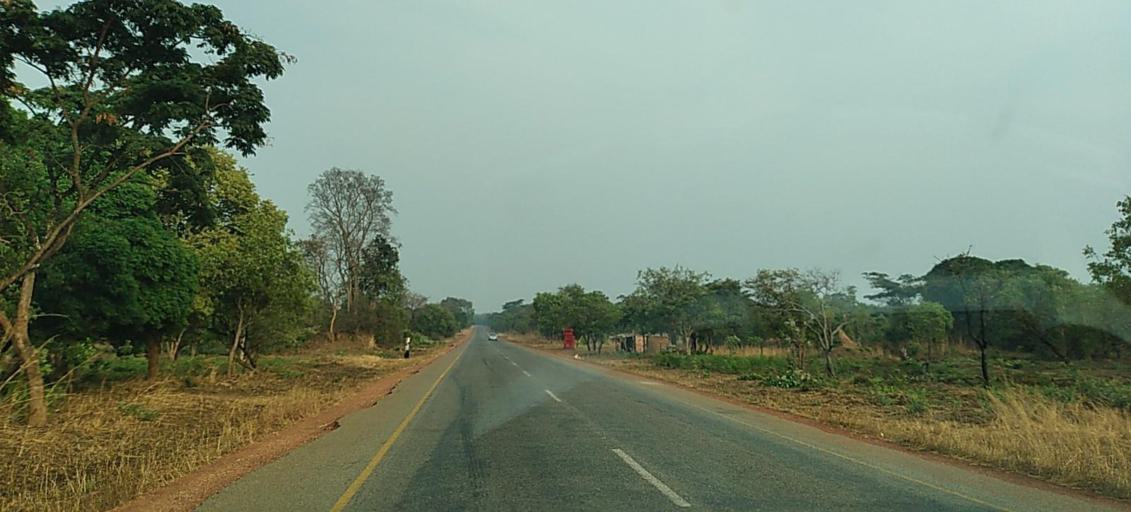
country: ZM
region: North-Western
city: Solwezi
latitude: -12.3862
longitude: 26.0303
